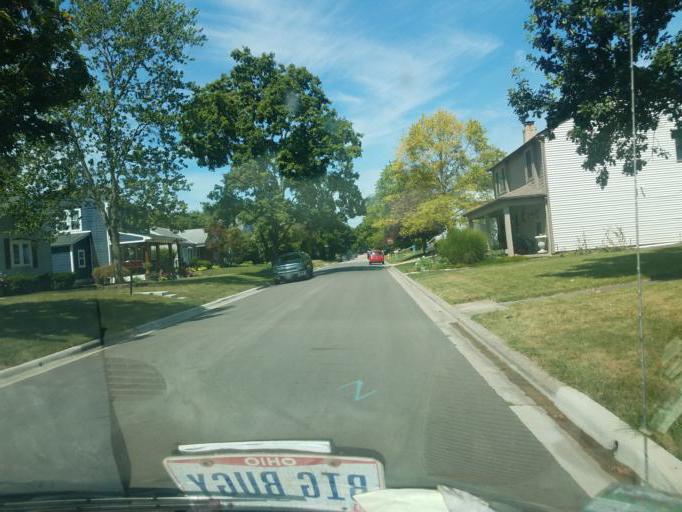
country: US
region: Ohio
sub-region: Franklin County
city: Grove City
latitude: 39.8792
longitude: -83.0906
